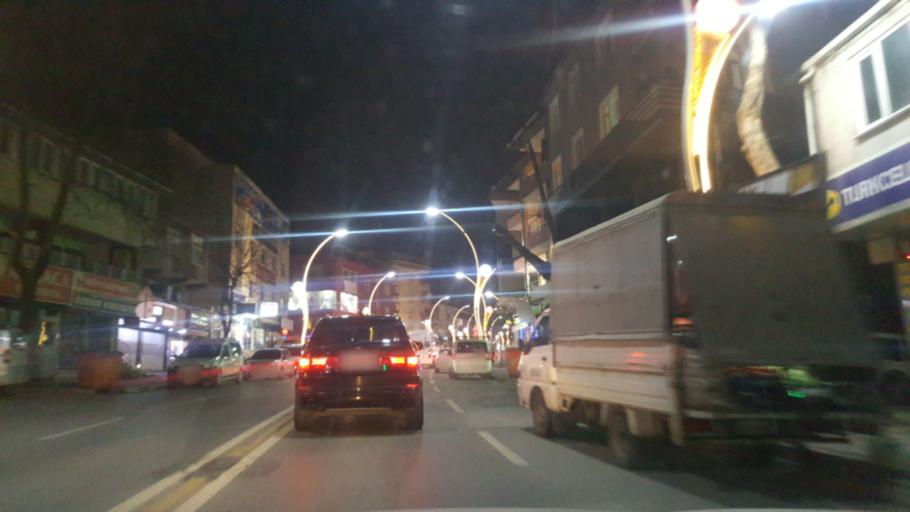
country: TR
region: Kocaeli
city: Darica
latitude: 40.7773
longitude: 29.4048
